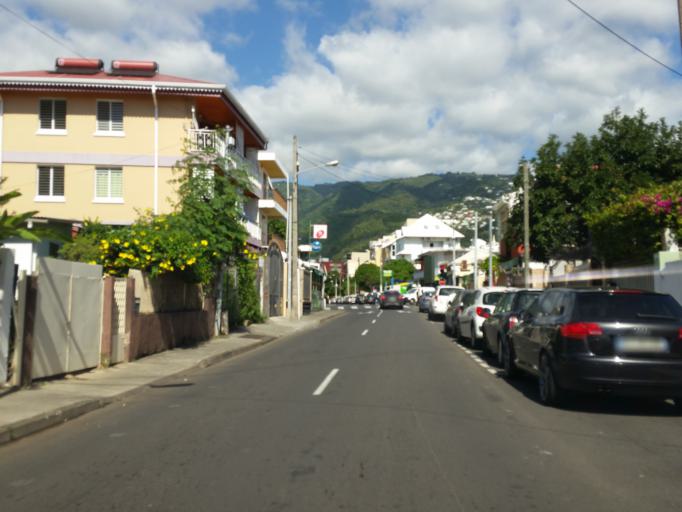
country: RE
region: Reunion
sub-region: Reunion
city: Saint-Denis
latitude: -20.8863
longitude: 55.4589
